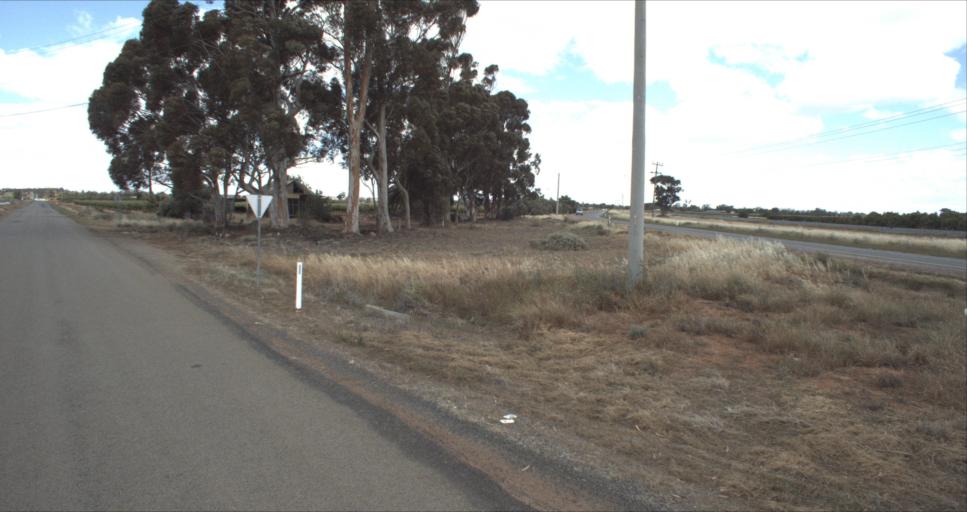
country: AU
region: New South Wales
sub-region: Leeton
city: Leeton
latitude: -34.5799
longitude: 146.3996
